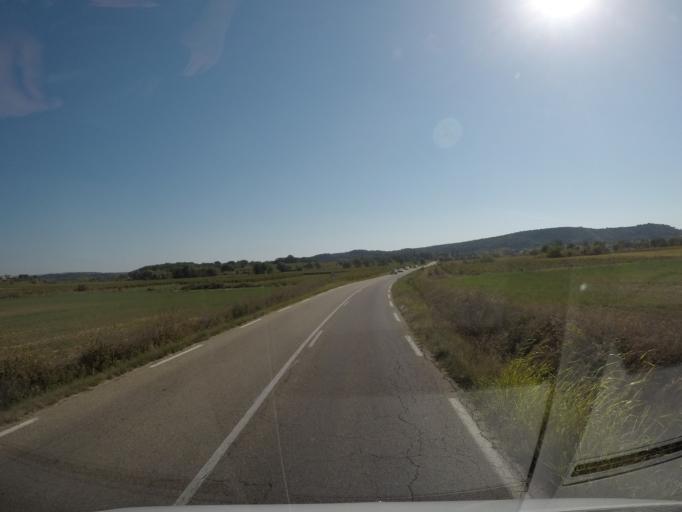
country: FR
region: Languedoc-Roussillon
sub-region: Departement du Gard
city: Ledignan
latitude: 44.0103
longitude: 4.1146
